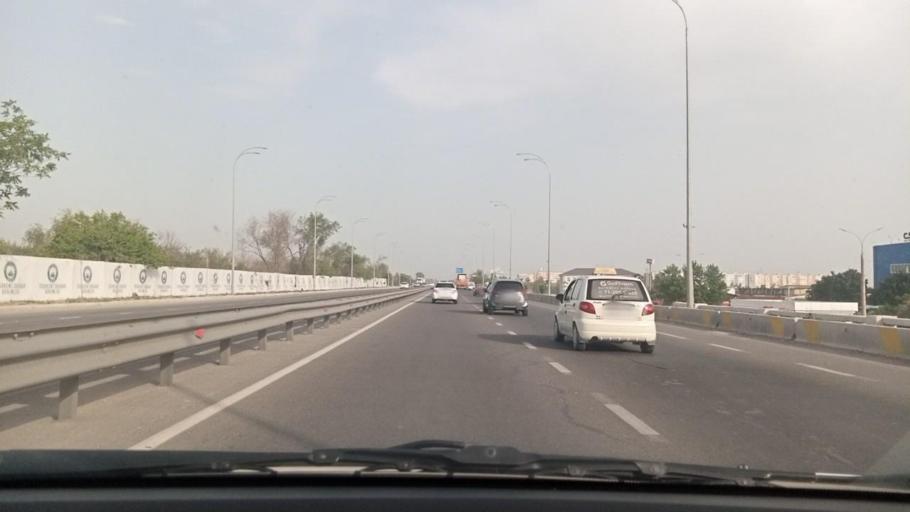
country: UZ
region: Toshkent Shahri
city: Bektemir
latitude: 41.2643
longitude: 69.3716
